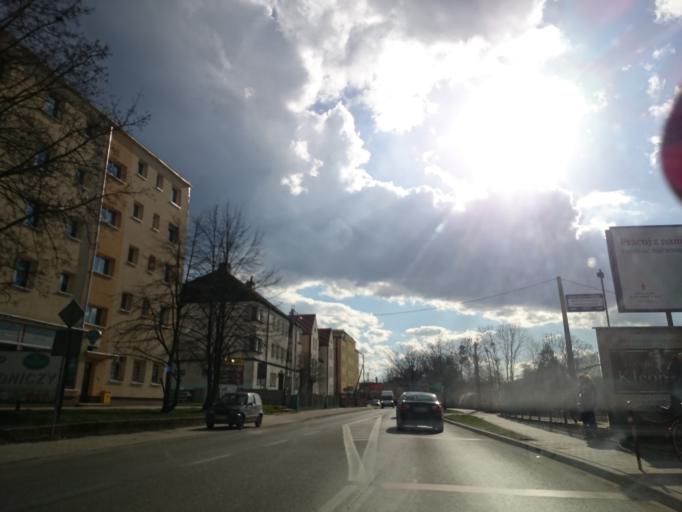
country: PL
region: Opole Voivodeship
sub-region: Powiat opolski
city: Niemodlin
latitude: 50.6406
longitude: 17.6293
